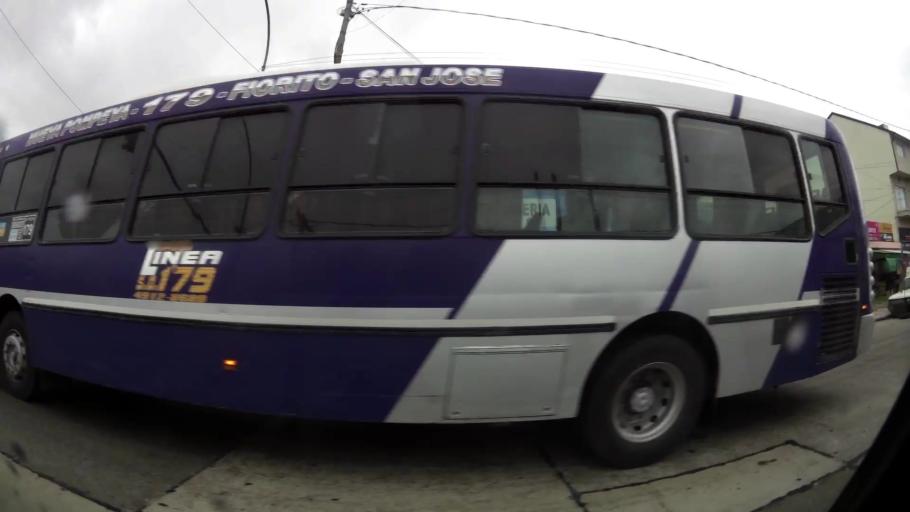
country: AR
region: Buenos Aires
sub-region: Partido de Lanus
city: Lanus
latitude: -34.6900
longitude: -58.4024
